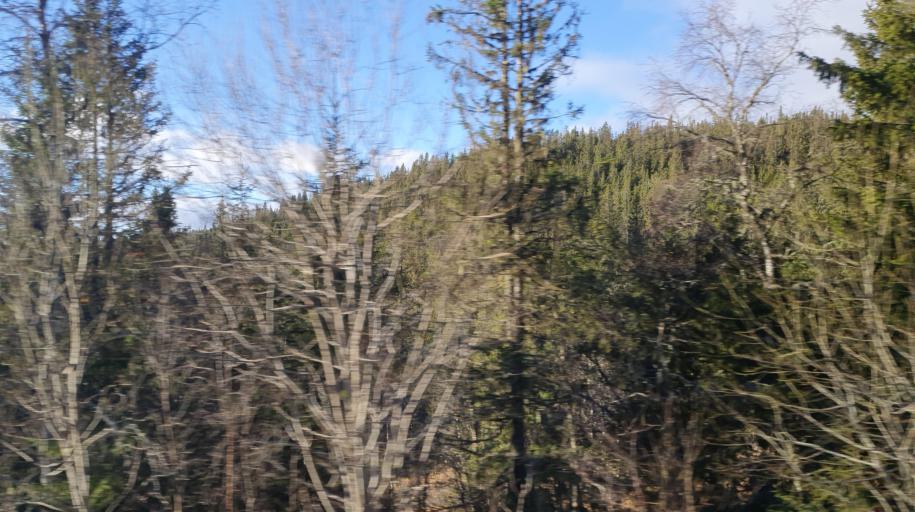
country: NO
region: Buskerud
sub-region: Krodsherad
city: Noresund
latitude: 60.2225
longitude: 9.5320
